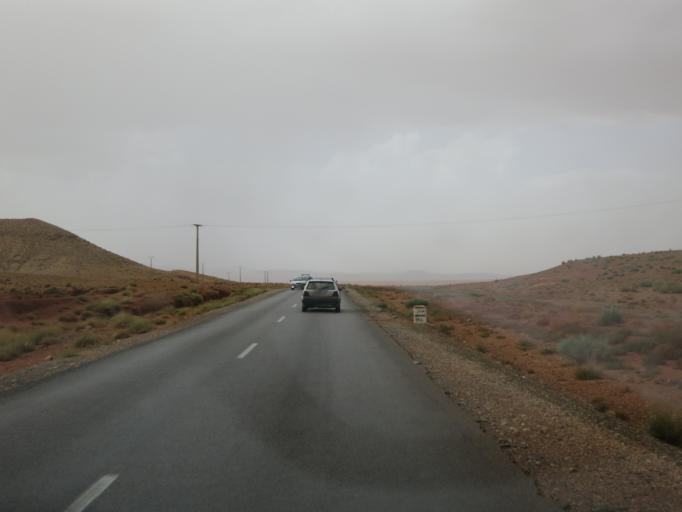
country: MA
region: Meknes-Tafilalet
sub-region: Khenifra
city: Itzer
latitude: 32.8641
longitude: -4.9448
